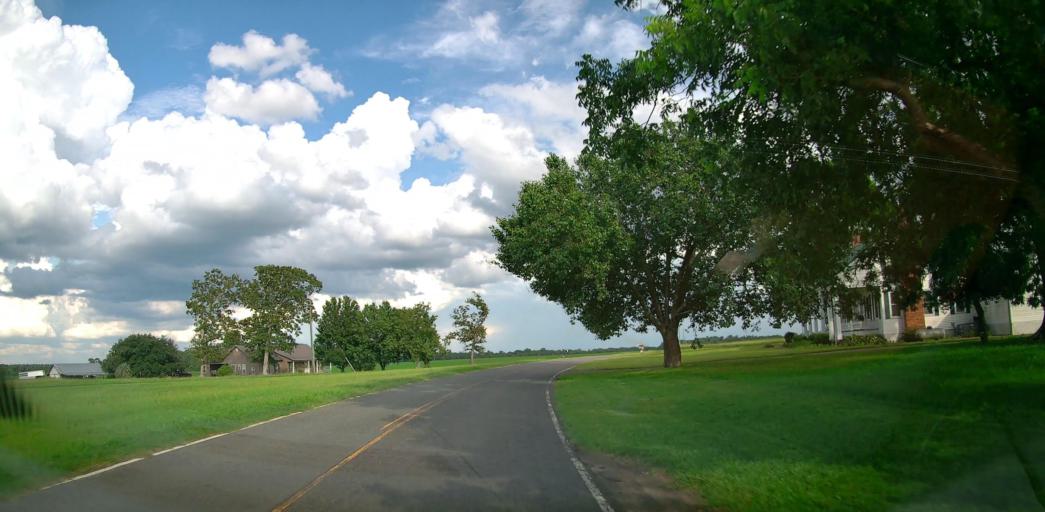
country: US
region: Georgia
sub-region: Bleckley County
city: Cochran
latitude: 32.4088
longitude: -83.4275
